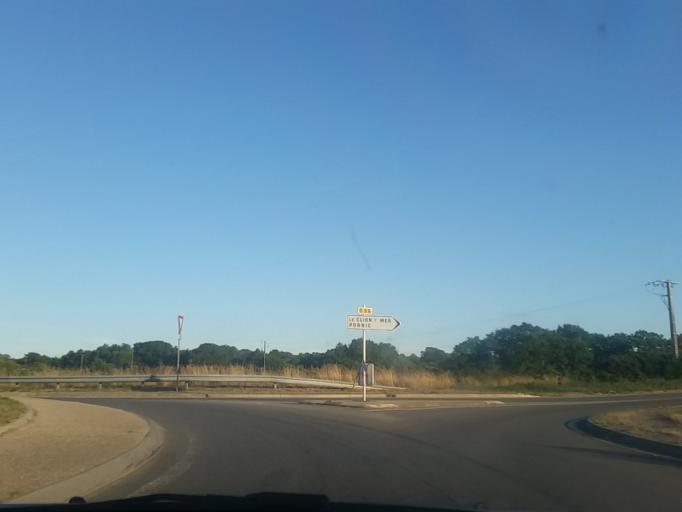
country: FR
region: Pays de la Loire
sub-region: Departement de la Loire-Atlantique
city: Saint-Pere-en-Retz
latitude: 47.2021
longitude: -2.0494
